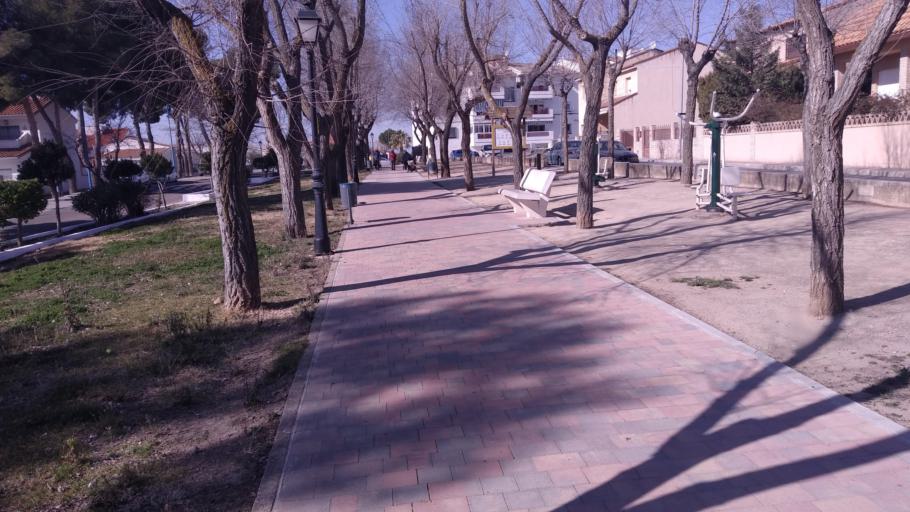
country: ES
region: Castille-La Mancha
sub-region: Province of Toledo
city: Esquivias
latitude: 40.1026
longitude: -3.7600
